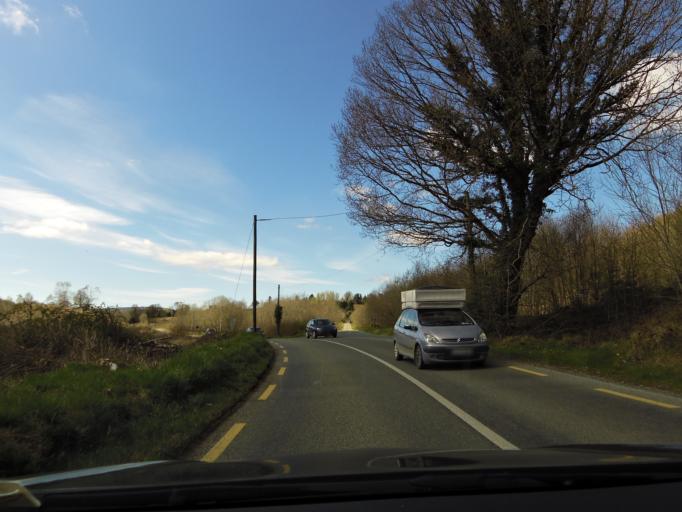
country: IE
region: Leinster
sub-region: Wicklow
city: Aughrim
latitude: 52.8485
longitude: -6.2762
